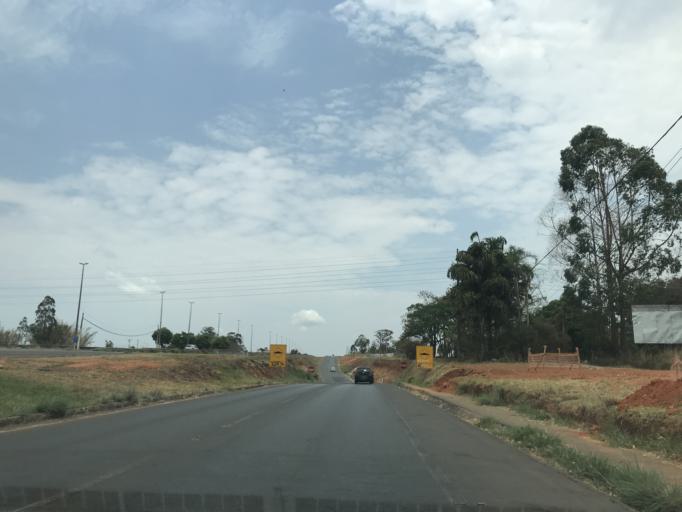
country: BR
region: Federal District
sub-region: Brasilia
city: Brasilia
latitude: -15.6697
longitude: -47.8158
